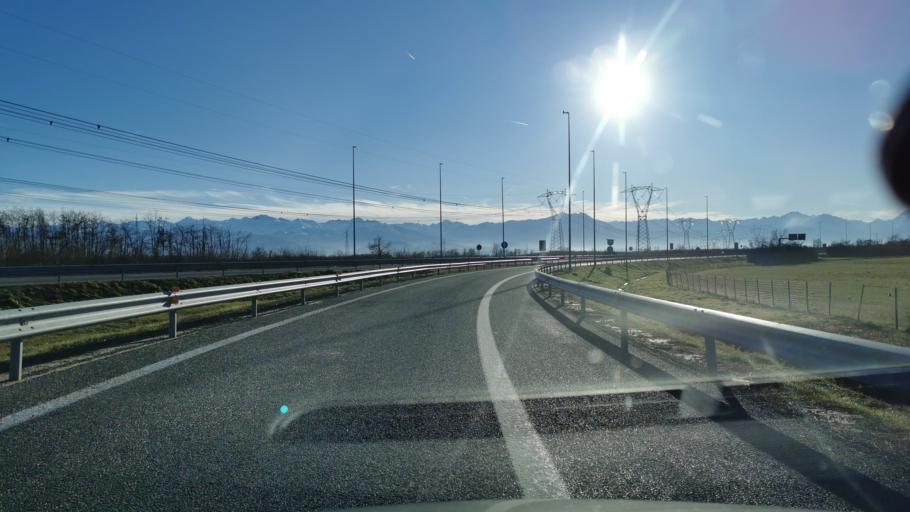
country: IT
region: Piedmont
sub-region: Provincia di Cuneo
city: Magliano Alpi
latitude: 44.4873
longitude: 7.8155
